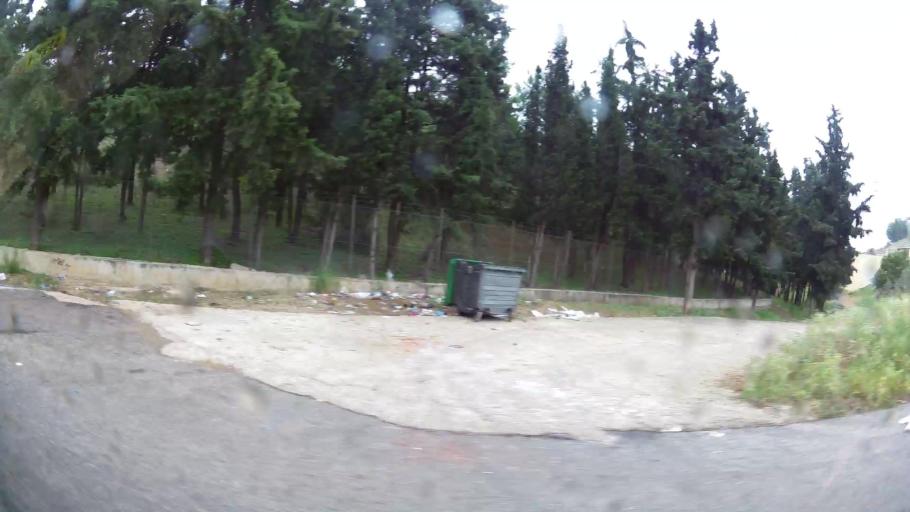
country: GR
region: Attica
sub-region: Nomos Piraios
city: Korydallos
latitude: 37.9980
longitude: 23.6489
